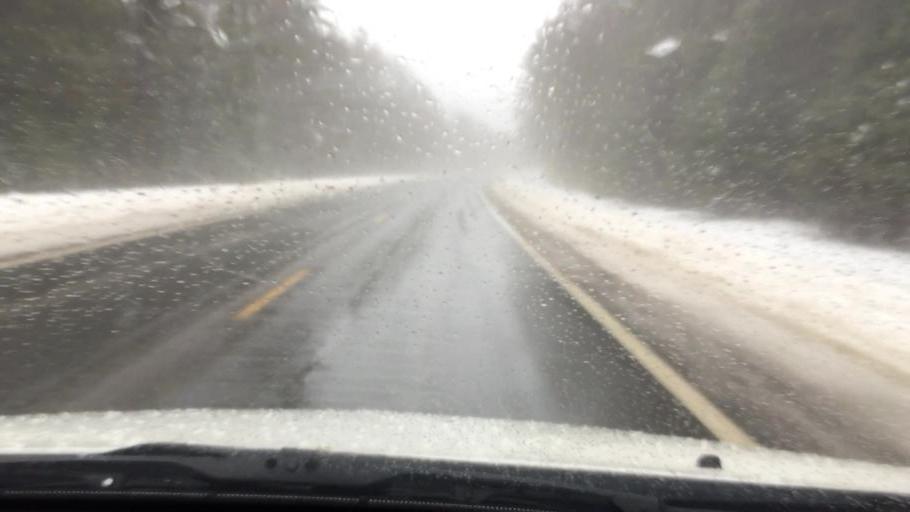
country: US
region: Michigan
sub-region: Charlevoix County
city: East Jordan
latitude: 45.0529
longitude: -85.0714
